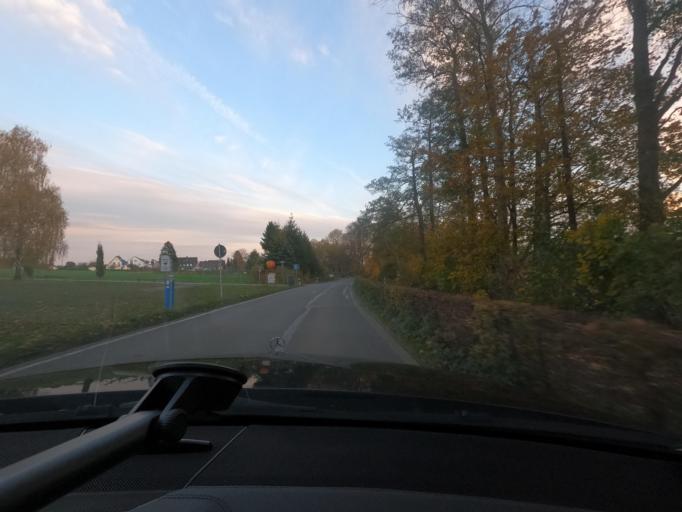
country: DE
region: North Rhine-Westphalia
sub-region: Regierungsbezirk Arnsberg
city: Mohnesee
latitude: 51.4935
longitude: 8.1515
